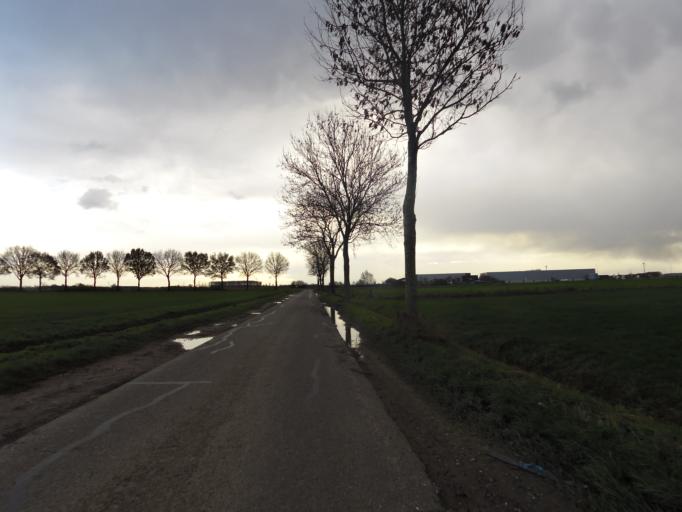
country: NL
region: Gelderland
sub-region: Gemeente Montferland
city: s-Heerenberg
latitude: 51.8804
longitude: 6.2812
